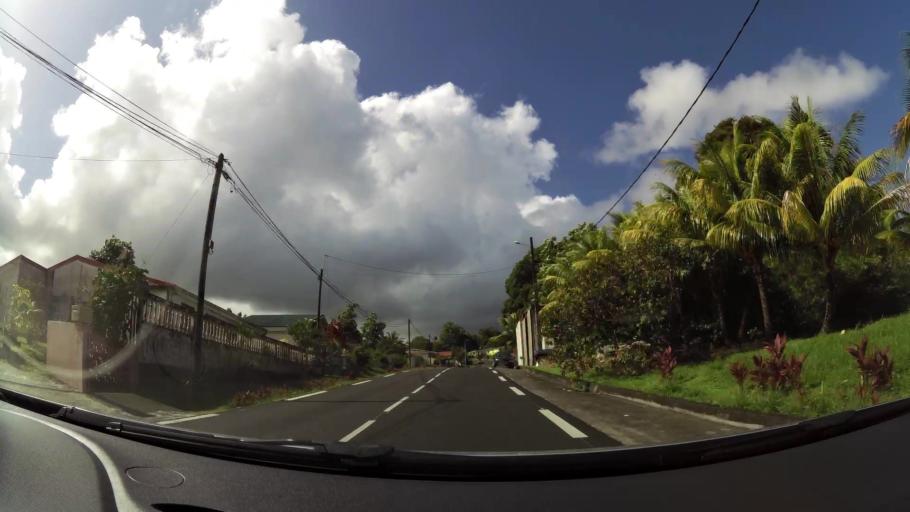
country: MQ
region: Martinique
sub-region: Martinique
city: Basse-Pointe
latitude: 14.8303
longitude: -61.1068
